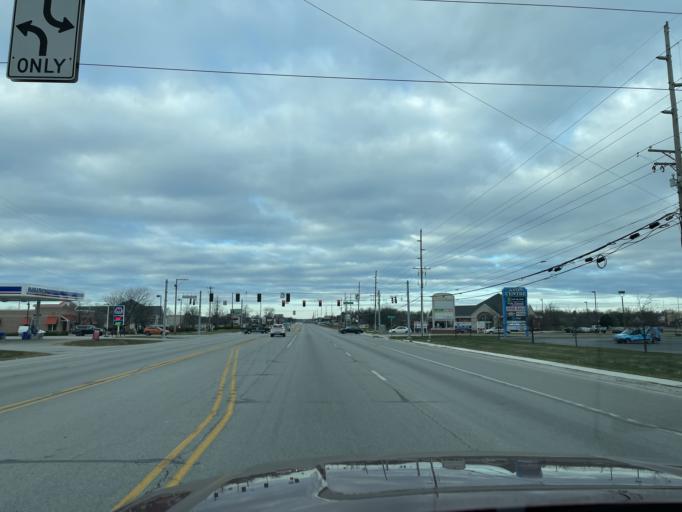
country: US
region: Indiana
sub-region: Hendricks County
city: Avon
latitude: 39.7630
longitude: -86.3860
